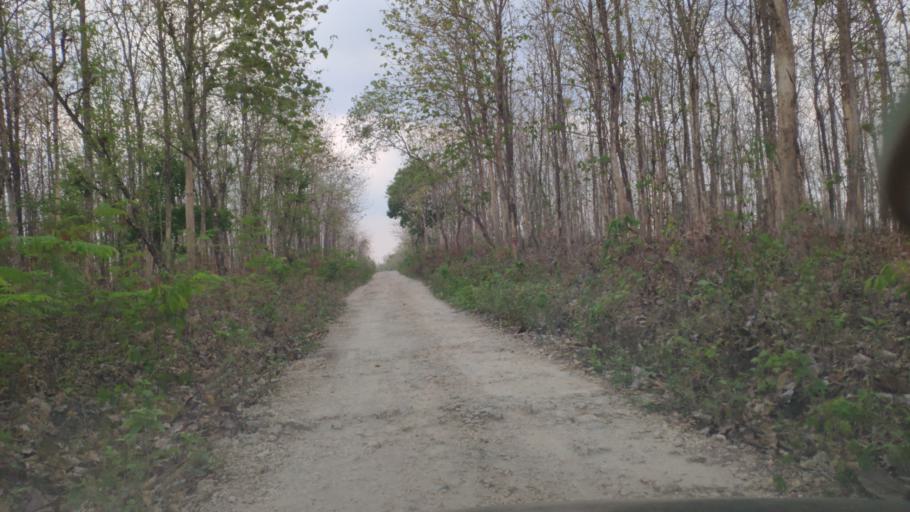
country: ID
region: Central Java
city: Randublatung
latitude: -7.2800
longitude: 111.2886
